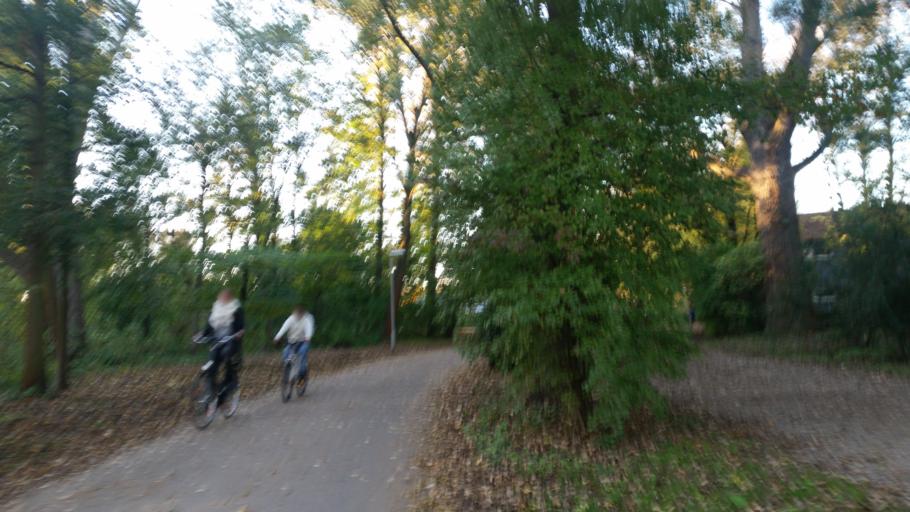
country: DE
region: Lower Saxony
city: Hannover
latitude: 52.3531
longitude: 9.7403
